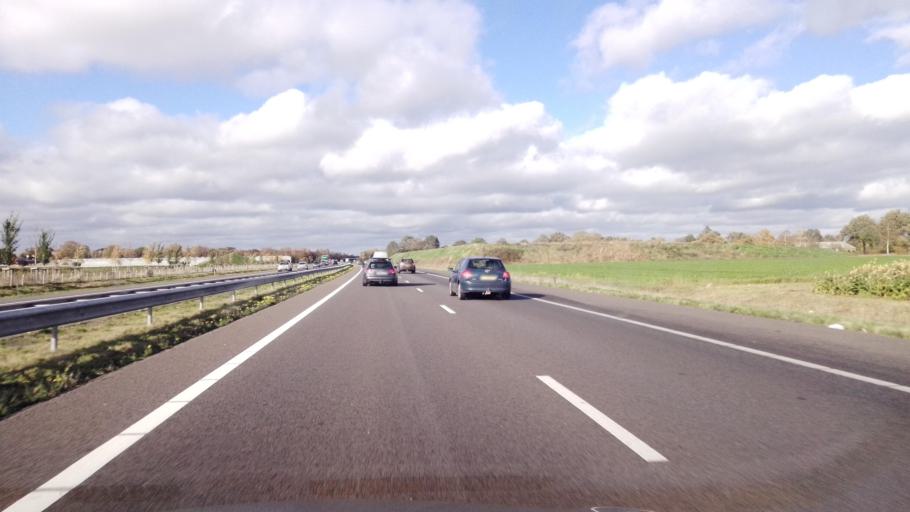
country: NL
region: Limburg
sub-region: Gemeente Peel en Maas
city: Maasbree
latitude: 51.4369
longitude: 6.0939
